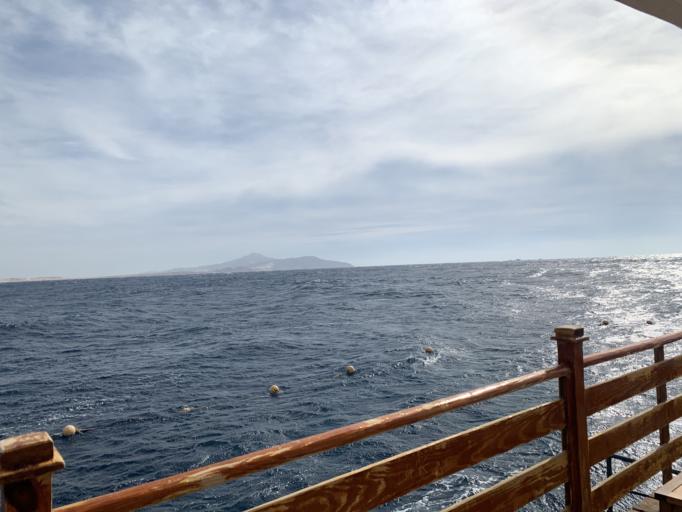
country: EG
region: South Sinai
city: Sharm el-Sheikh
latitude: 28.0206
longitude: 34.4416
